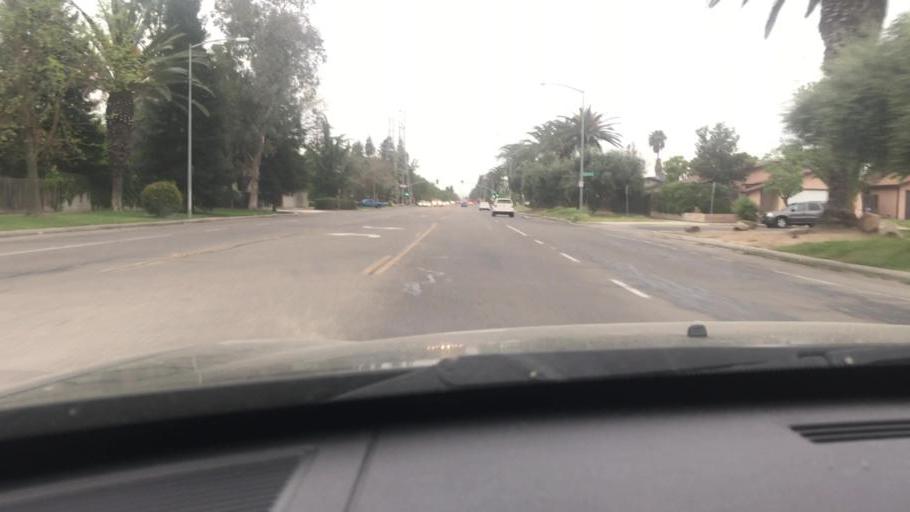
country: US
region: California
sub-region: Fresno County
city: West Park
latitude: 36.8160
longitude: -119.8692
